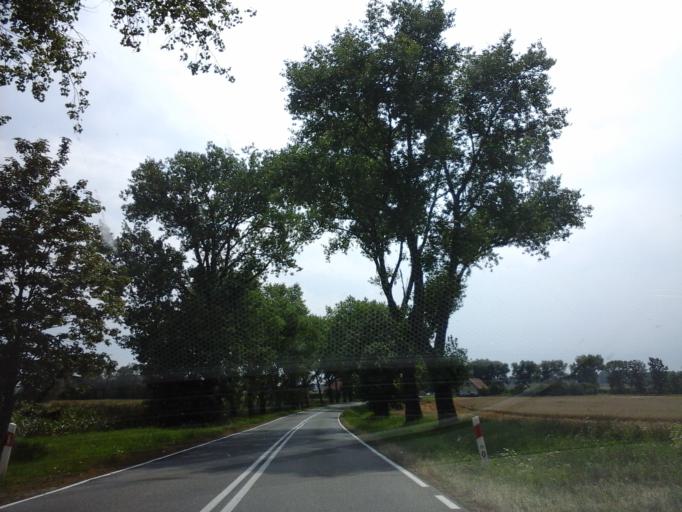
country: PL
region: Lower Silesian Voivodeship
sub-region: Powiat strzelinski
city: Strzelin
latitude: 50.8432
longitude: 17.0591
